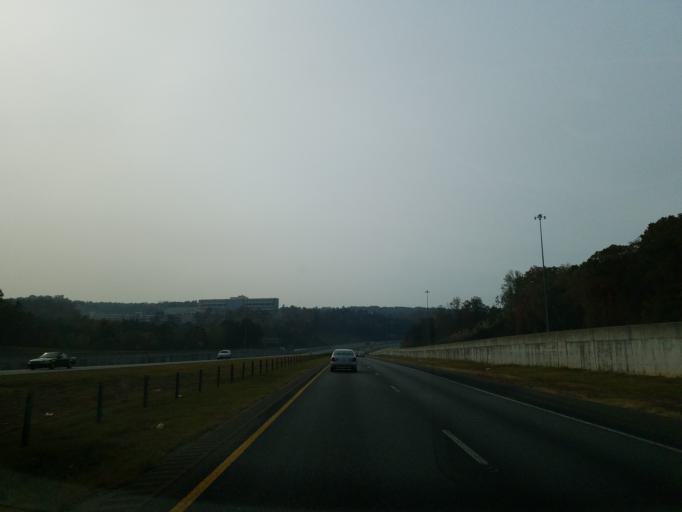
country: US
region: Georgia
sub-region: Cherokee County
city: Canton
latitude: 34.2368
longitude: -84.4665
